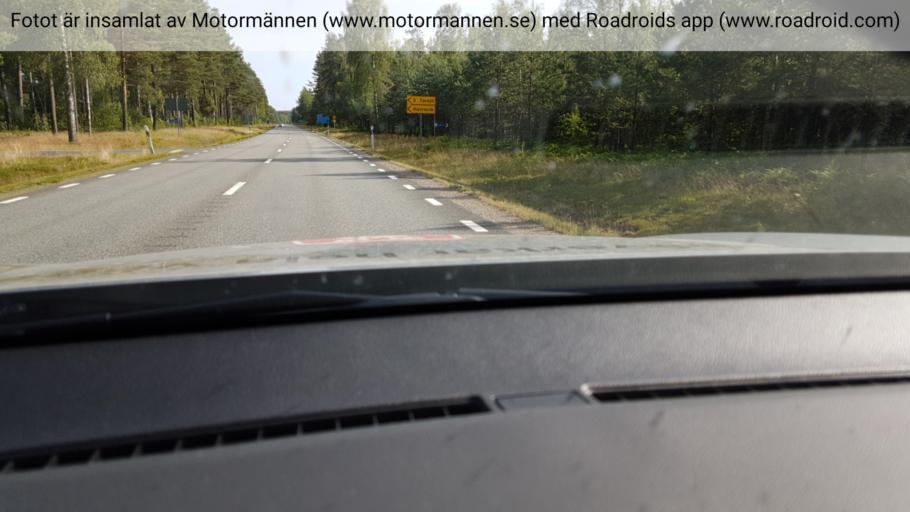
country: SE
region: Joenkoeping
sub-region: Eksjo Kommun
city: Eksjoe
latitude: 57.6075
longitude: 14.9692
